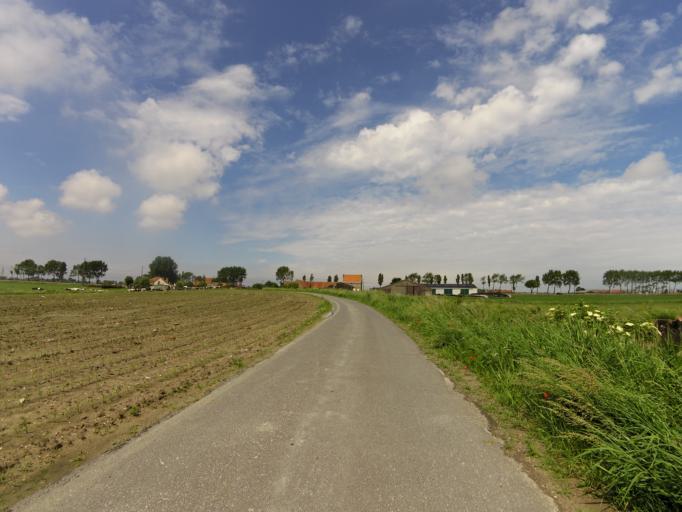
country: BE
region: Flanders
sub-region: Provincie West-Vlaanderen
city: Nieuwpoort
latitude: 51.1460
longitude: 2.7933
